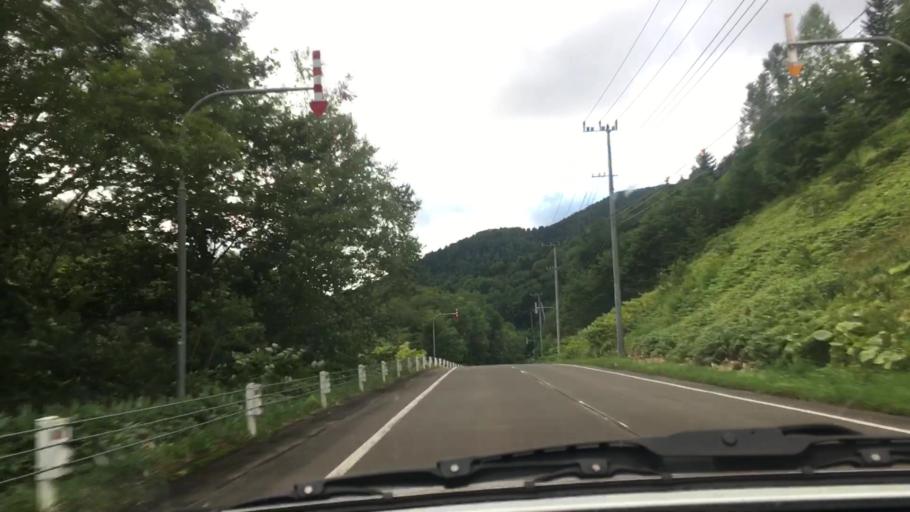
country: JP
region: Hokkaido
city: Shimo-furano
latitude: 43.0459
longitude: 142.5162
